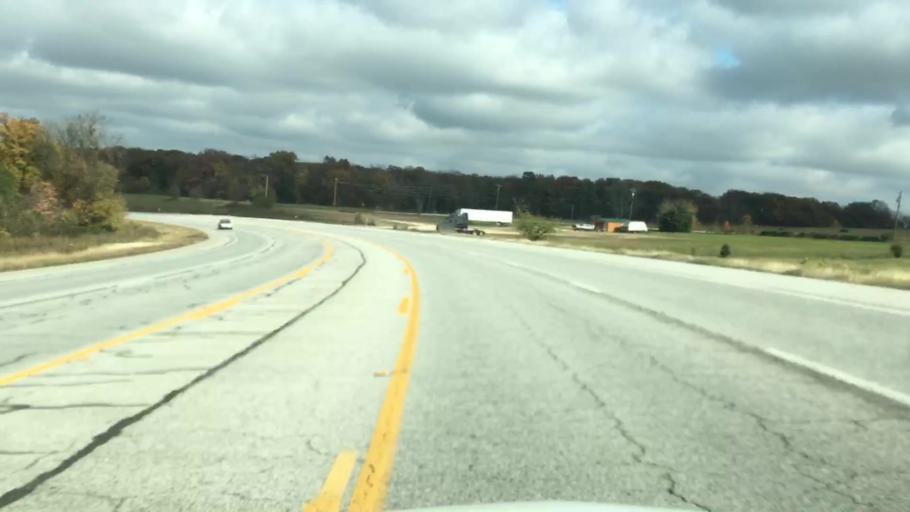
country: US
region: Arkansas
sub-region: Benton County
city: Gentry
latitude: 36.2360
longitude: -94.4883
